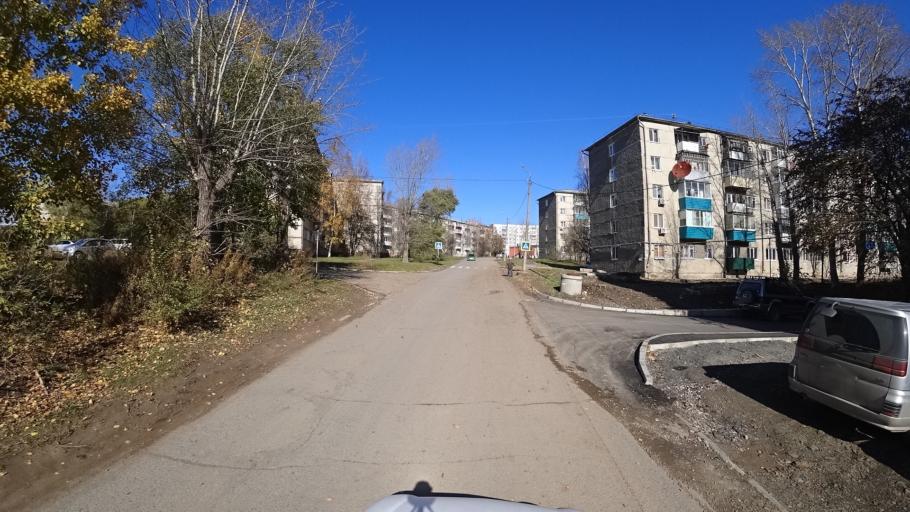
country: RU
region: Khabarovsk Krai
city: Amursk
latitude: 50.2159
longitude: 136.8924
